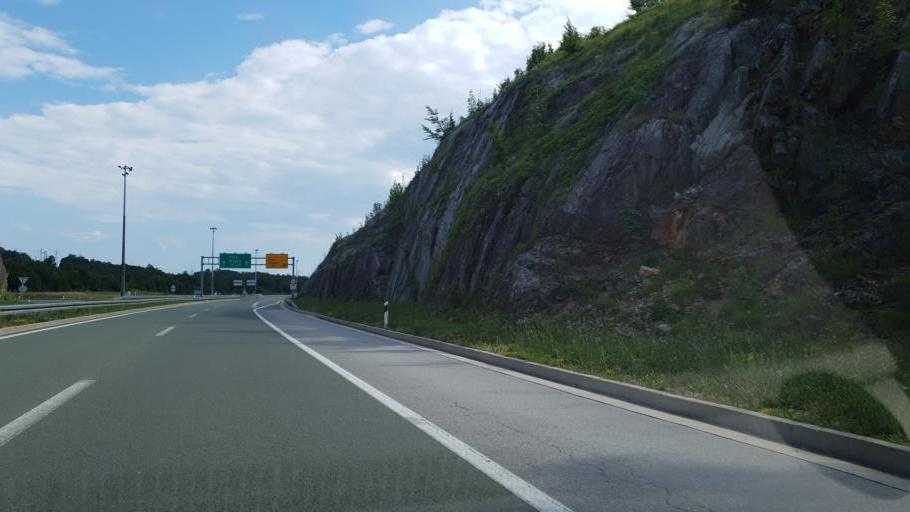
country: HR
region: Primorsko-Goranska
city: Matulji
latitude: 45.3996
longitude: 14.3005
